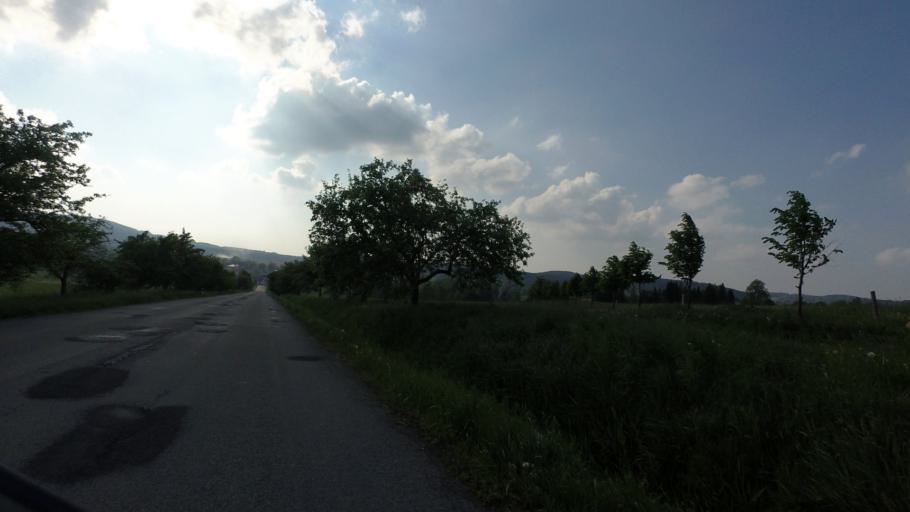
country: CZ
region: Ustecky
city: Velky Senov
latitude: 51.0095
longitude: 14.3681
